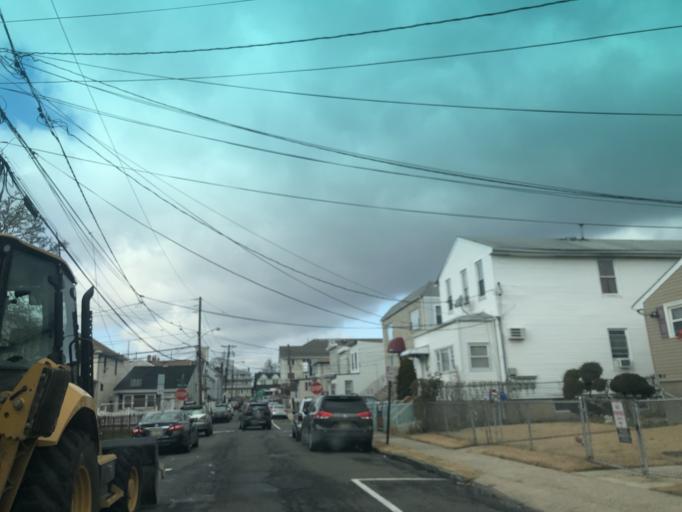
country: US
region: New Jersey
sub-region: Hudson County
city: Union City
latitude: 40.7848
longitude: -74.0309
